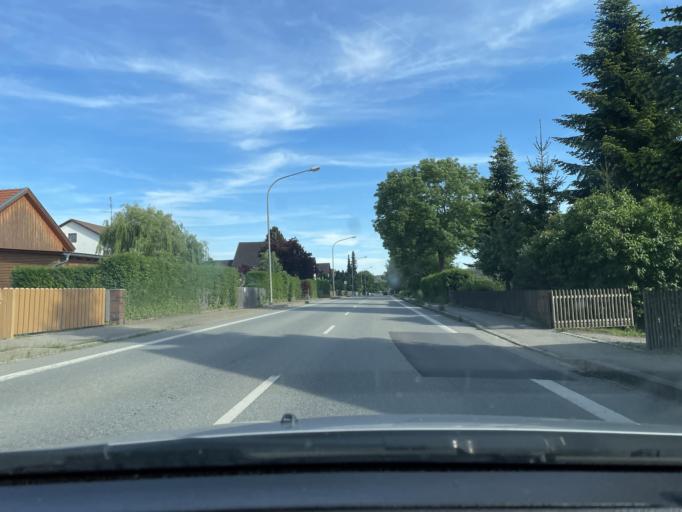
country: DE
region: Bavaria
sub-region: Lower Bavaria
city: Weihmichl
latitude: 48.5872
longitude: 12.0619
